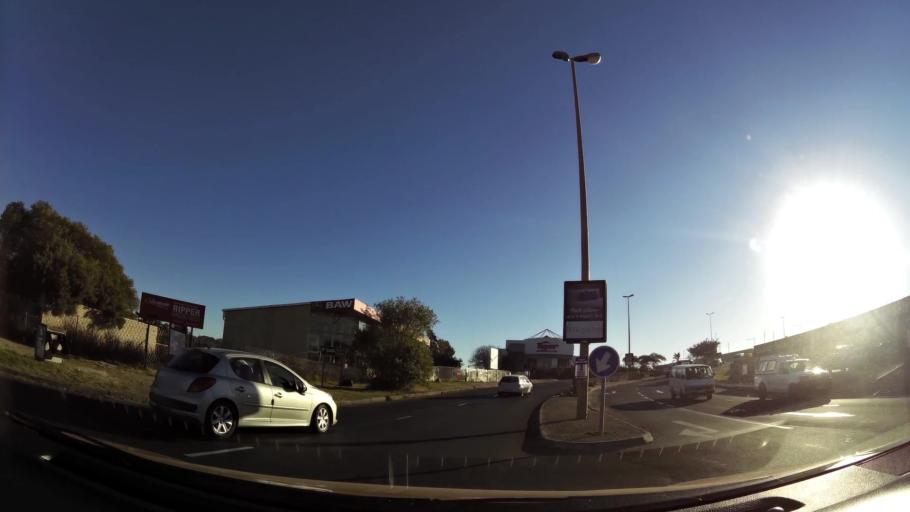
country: ZA
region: Gauteng
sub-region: City of Johannesburg Metropolitan Municipality
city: Midrand
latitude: -25.9892
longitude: 28.1306
